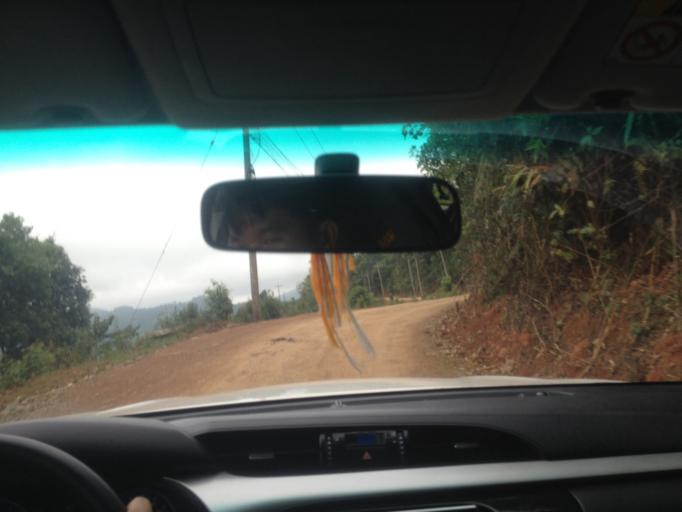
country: TH
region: Nan
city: Chaloem Phra Kiat
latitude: 19.9926
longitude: 101.1378
